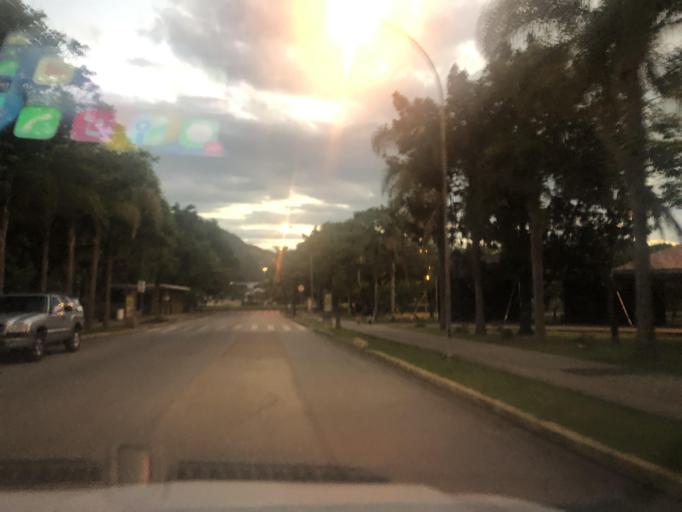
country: BR
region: Santa Catarina
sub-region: Florianopolis
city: Carvoeira
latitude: -27.5991
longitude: -48.5205
